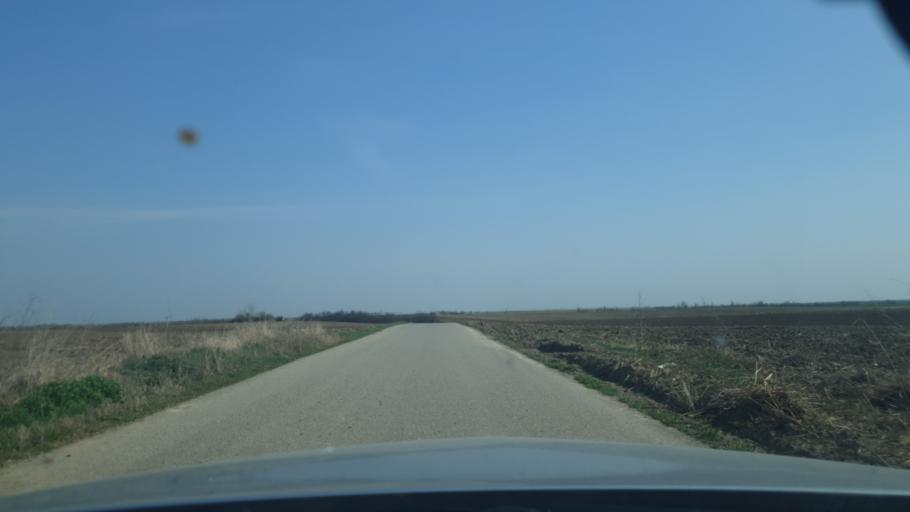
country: RS
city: Putinci
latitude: 45.0530
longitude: 19.9366
